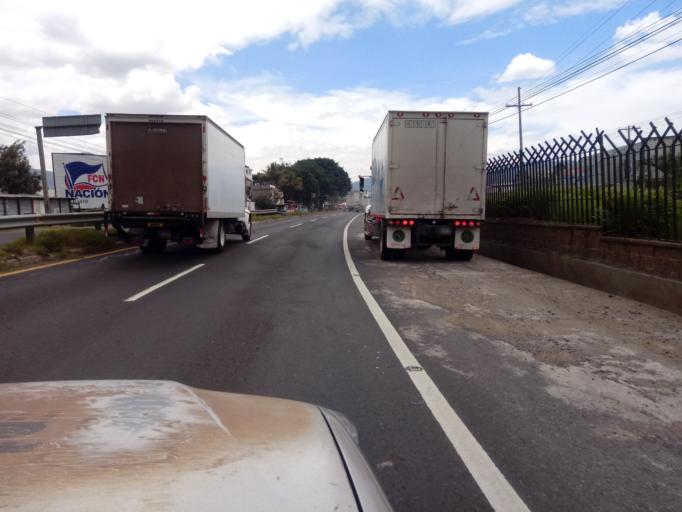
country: GT
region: Guatemala
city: Amatitlan
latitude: 14.4602
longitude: -90.6430
